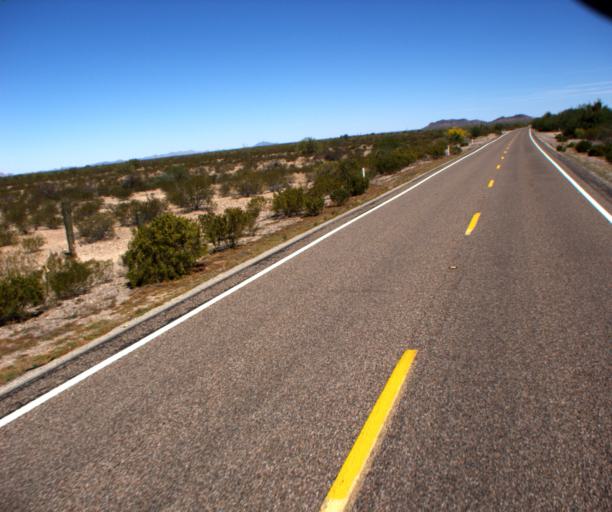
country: MX
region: Sonora
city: Sonoyta
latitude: 32.0243
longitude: -112.8017
